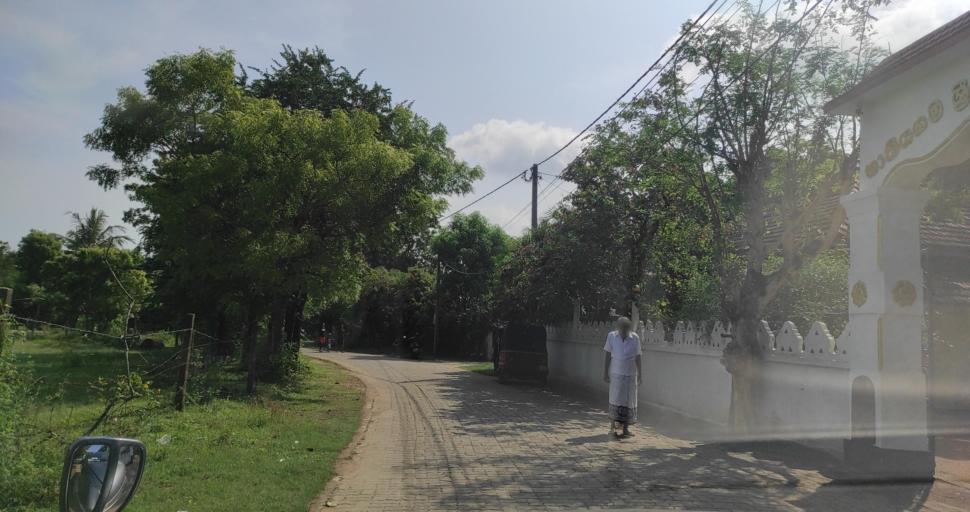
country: LK
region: Eastern Province
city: Trincomalee
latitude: 8.3795
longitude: 81.0139
